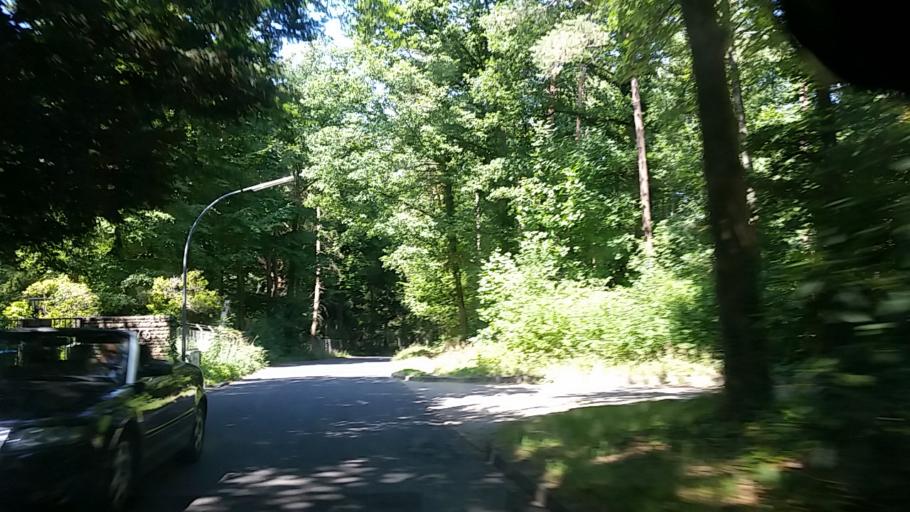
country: DE
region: Schleswig-Holstein
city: Wedel
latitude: 53.5696
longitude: 9.7656
